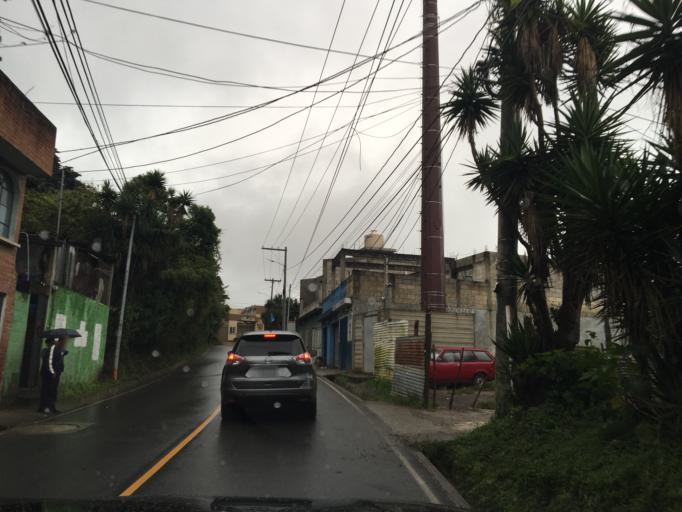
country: GT
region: Guatemala
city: Santa Catarina Pinula
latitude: 14.5599
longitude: -90.5001
